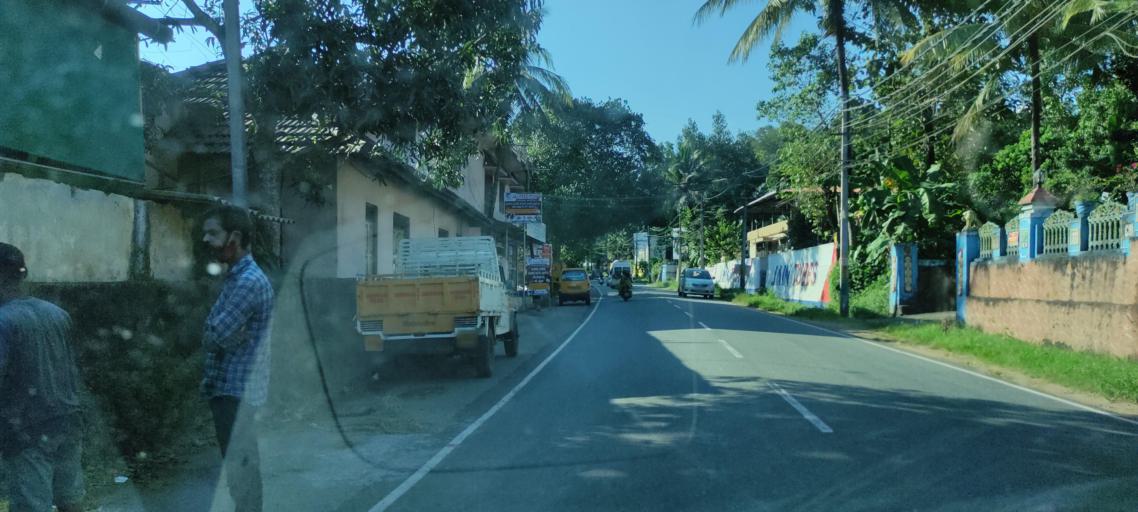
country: IN
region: Kerala
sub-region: Pattanamtitta
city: Pathanamthitta
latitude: 9.2546
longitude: 76.7656
